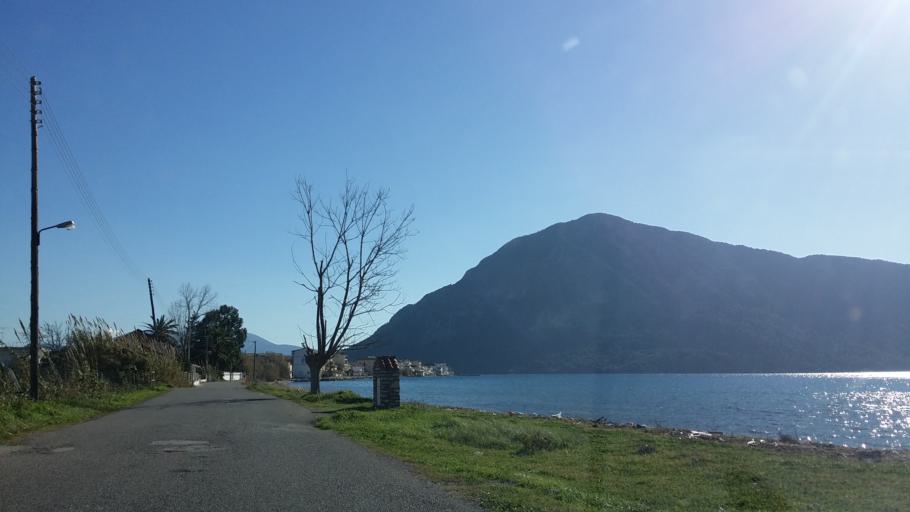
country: GR
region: West Greece
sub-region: Nomos Aitolias kai Akarnanias
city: Kandila
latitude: 38.6748
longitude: 20.9399
